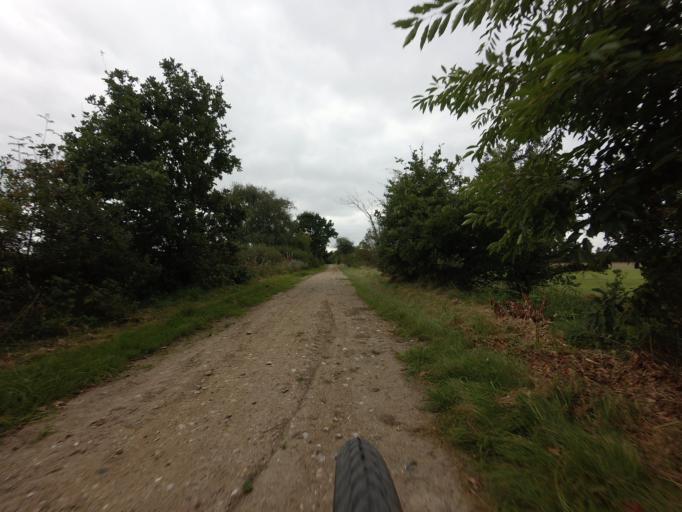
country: DK
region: Central Jutland
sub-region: Ikast-Brande Kommune
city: Brande
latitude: 55.9048
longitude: 9.0813
